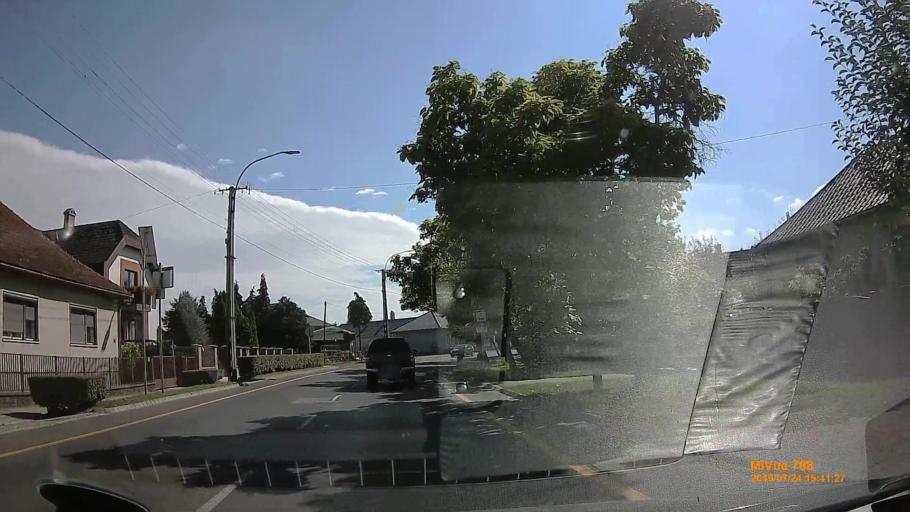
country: HU
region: Szabolcs-Szatmar-Bereg
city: Vasarosnameny
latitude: 48.1231
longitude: 22.3175
